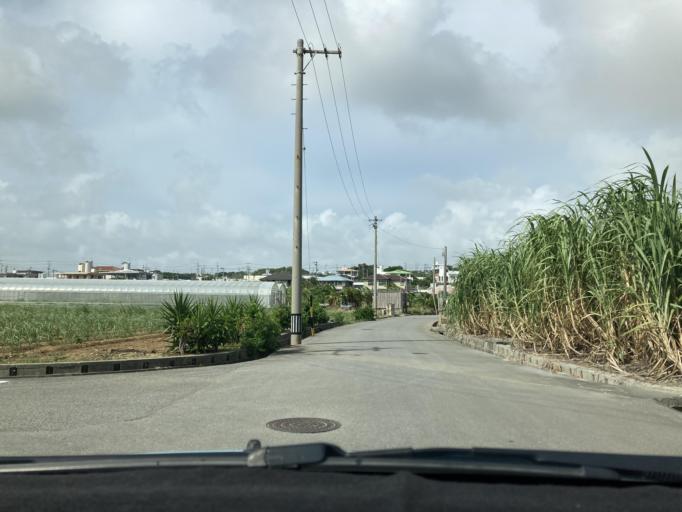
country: JP
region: Okinawa
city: Itoman
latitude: 26.0929
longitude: 127.7042
